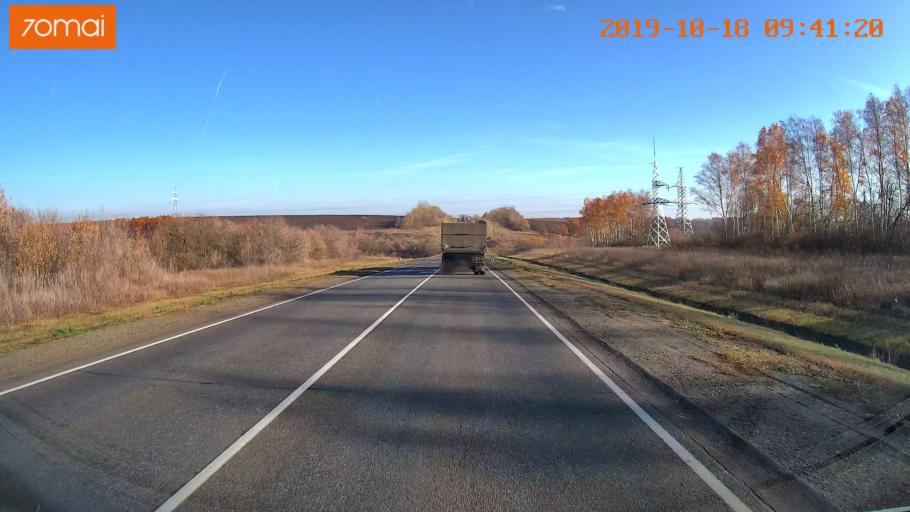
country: RU
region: Tula
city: Kazachka
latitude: 53.2738
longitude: 38.1604
